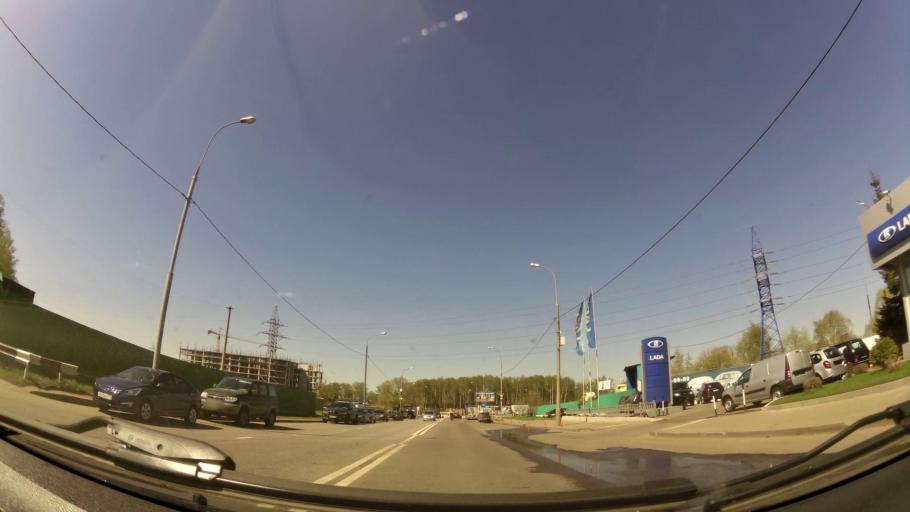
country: RU
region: Moscow
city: Strogino
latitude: 55.8011
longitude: 37.3874
